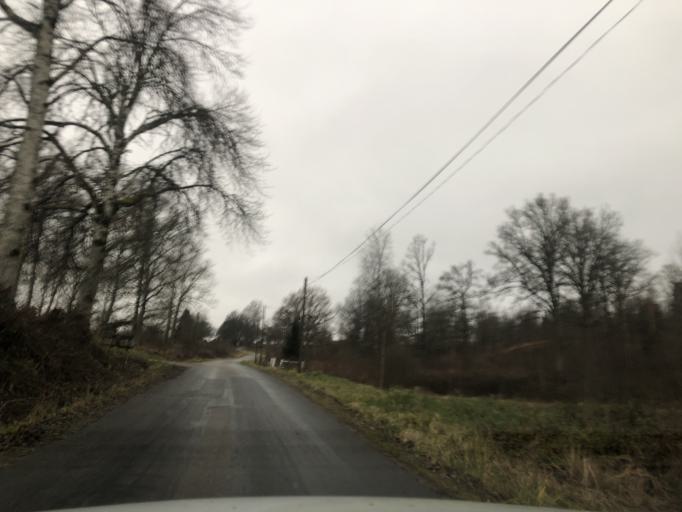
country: SE
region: Vaestra Goetaland
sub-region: Ulricehamns Kommun
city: Ulricehamn
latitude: 57.8882
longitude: 13.4308
